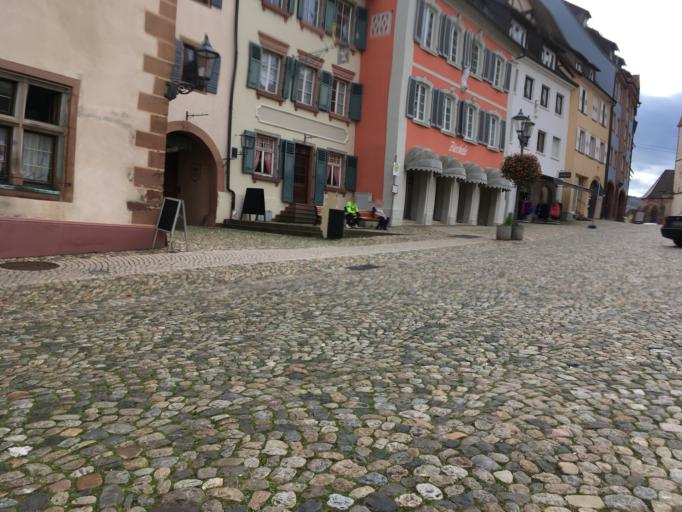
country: DE
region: Baden-Wuerttemberg
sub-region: Freiburg Region
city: Endingen
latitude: 48.1418
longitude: 7.7033
